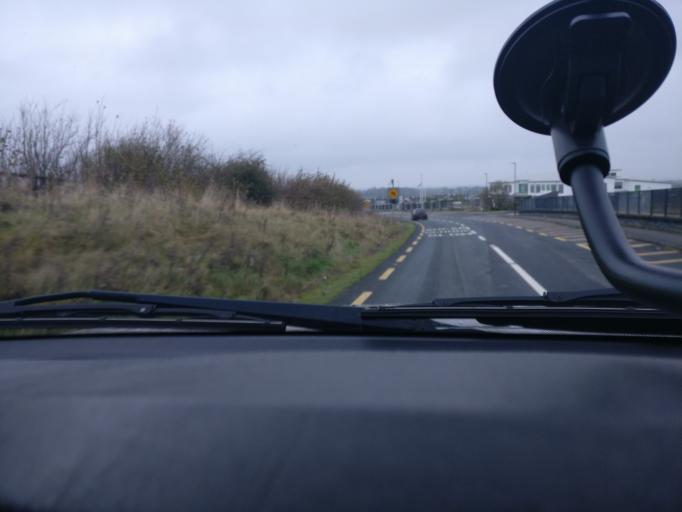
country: IE
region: Connaught
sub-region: County Galway
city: Loughrea
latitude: 53.2037
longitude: -8.5849
